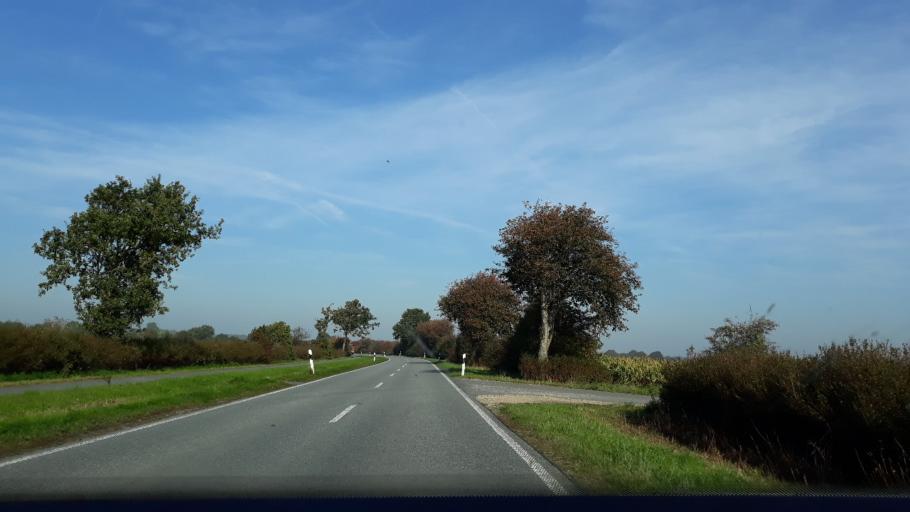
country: DE
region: Schleswig-Holstein
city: Dannewerk
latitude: 54.4681
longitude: 9.4911
